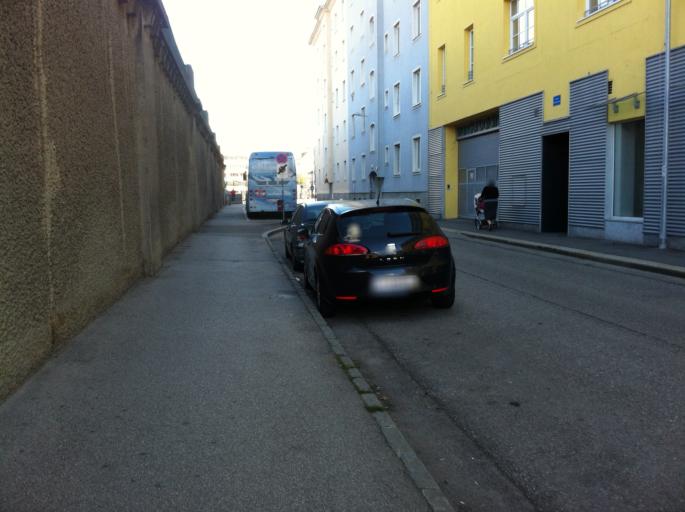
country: AT
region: Lower Austria
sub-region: Sankt Polten Stadt
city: Sankt Poelten
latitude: 48.2079
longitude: 15.6220
